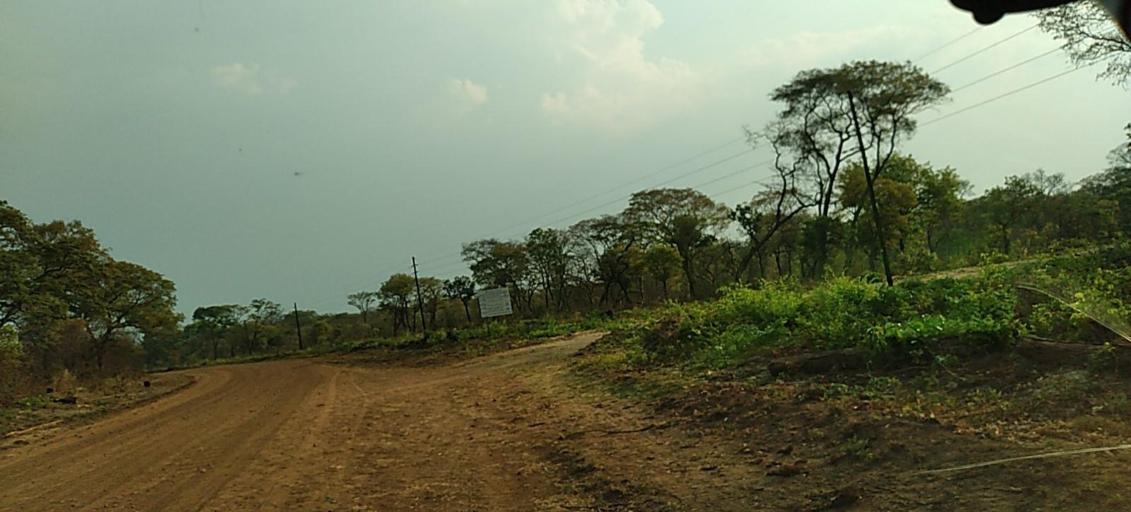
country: ZM
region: Western
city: Lukulu
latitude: -13.9936
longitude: 23.6156
